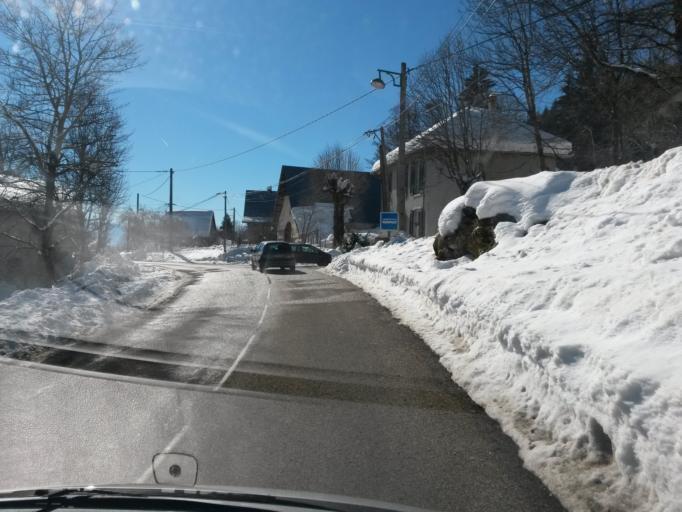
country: FR
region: Rhone-Alpes
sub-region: Departement de l'Isere
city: La Terrasse
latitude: 45.3446
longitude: 5.9057
